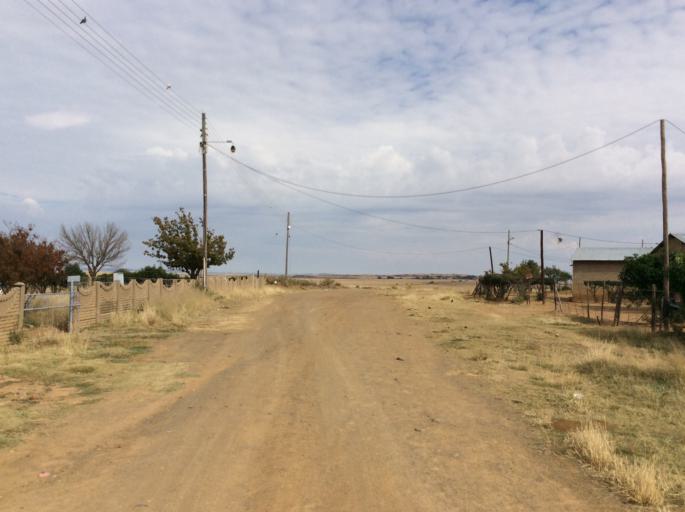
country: LS
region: Mafeteng
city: Mafeteng
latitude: -29.7241
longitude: 27.0106
